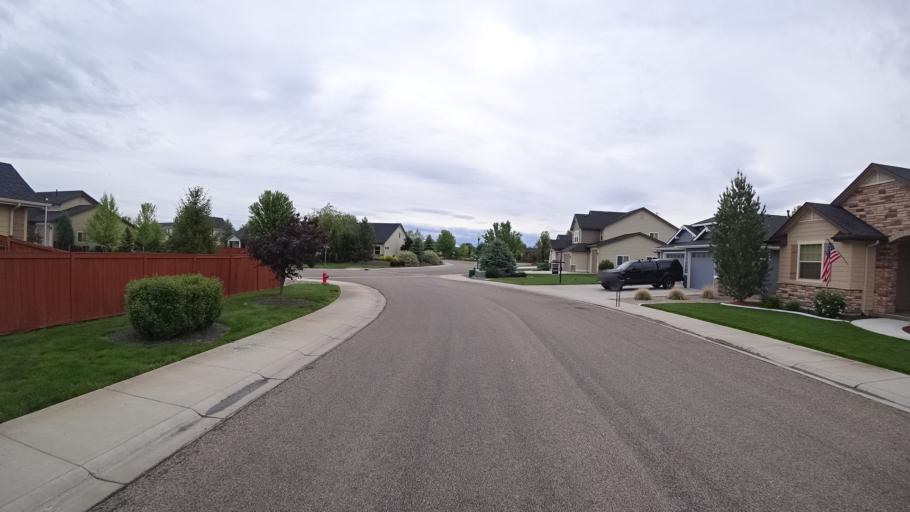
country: US
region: Idaho
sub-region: Ada County
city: Star
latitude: 43.6997
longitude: -116.4826
